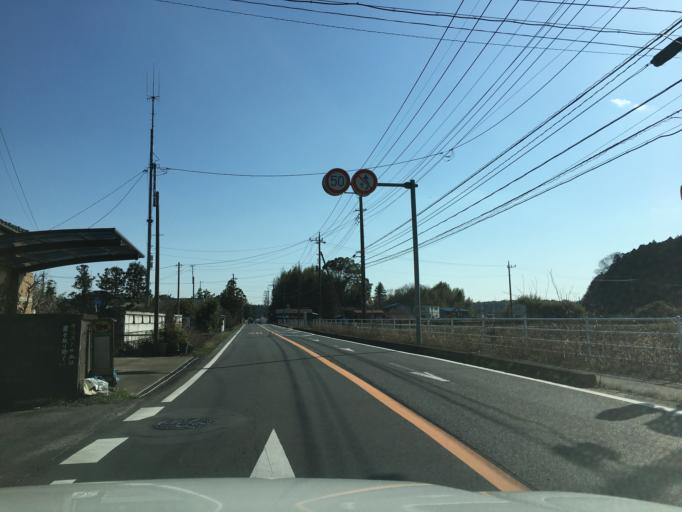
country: JP
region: Ibaraki
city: Omiya
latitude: 36.5039
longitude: 140.3721
